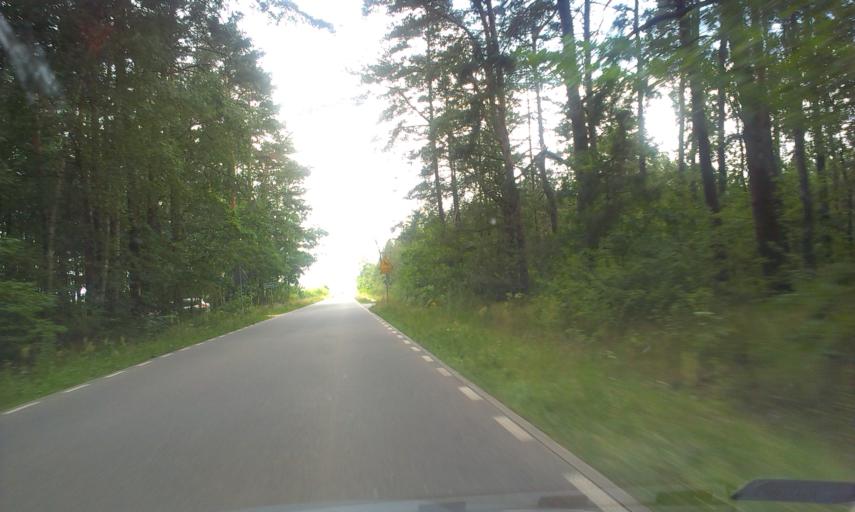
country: PL
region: Masovian Voivodeship
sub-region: Powiat zyrardowski
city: Radziejowice
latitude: 51.9690
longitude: 20.5836
